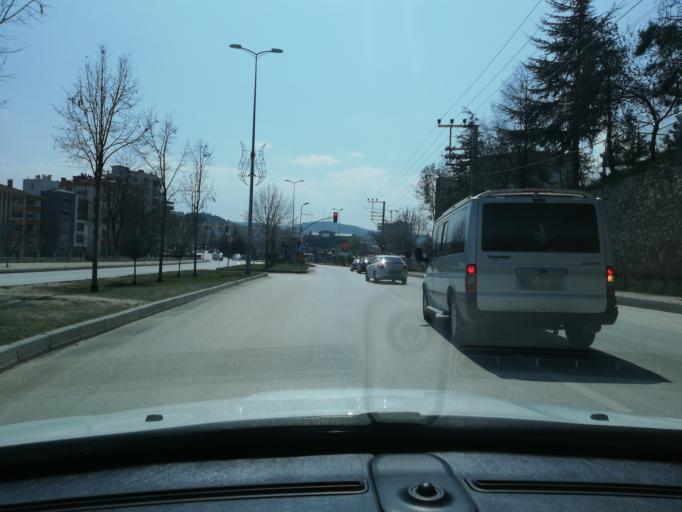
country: TR
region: Kastamonu
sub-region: Cide
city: Kastamonu
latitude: 41.3988
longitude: 33.7806
